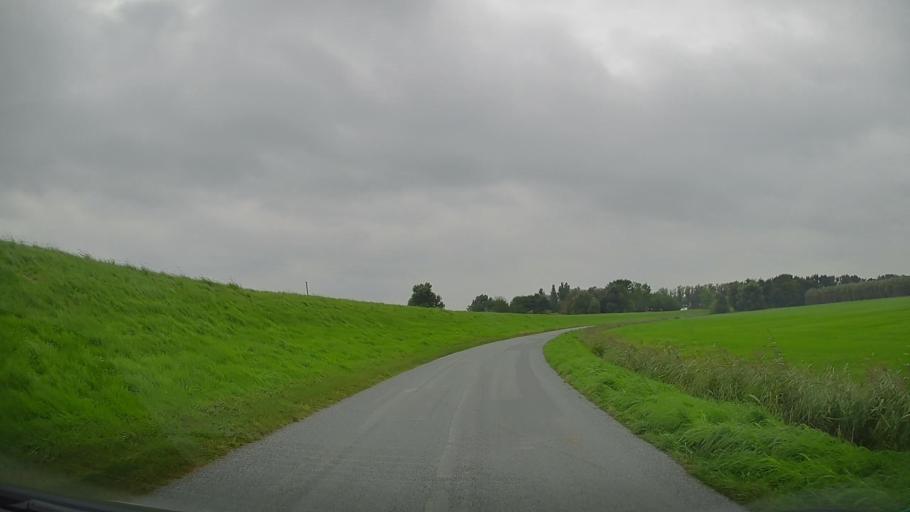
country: DE
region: Lower Saxony
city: Neuhaus an der Oste
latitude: 53.8102
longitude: 9.0358
